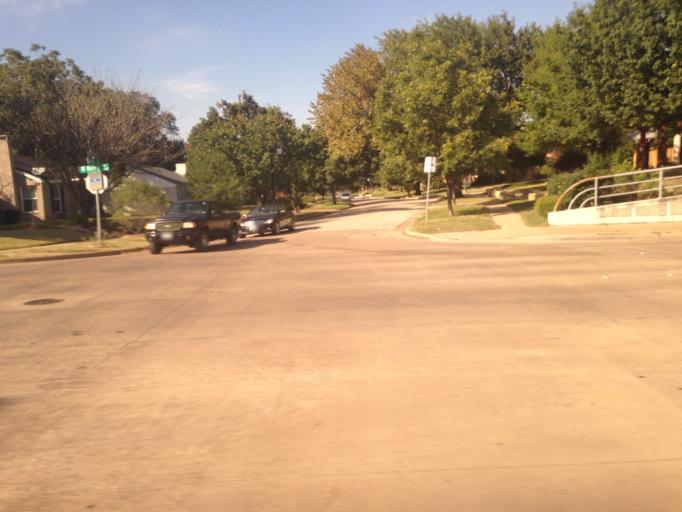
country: US
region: Texas
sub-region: Tarrant County
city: Fort Worth
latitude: 32.7060
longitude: -97.3412
